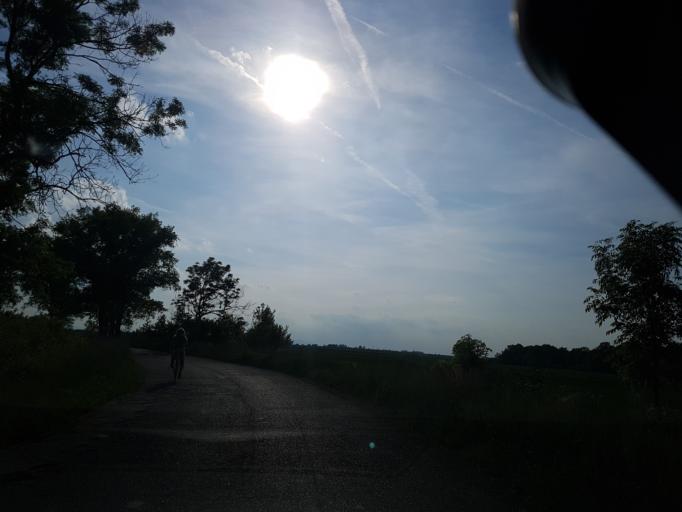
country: PL
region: Lower Silesian Voivodeship
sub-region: Powiat strzelinski
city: Wiazow
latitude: 50.8456
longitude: 17.2364
